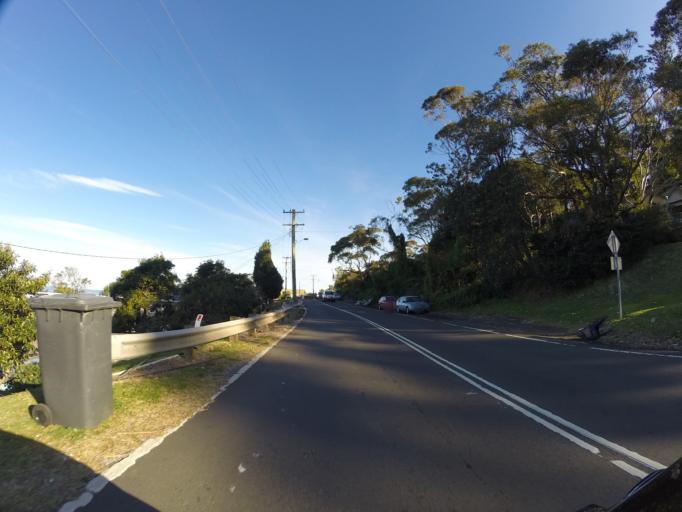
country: AU
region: New South Wales
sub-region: Wollongong
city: Bulli
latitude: -34.2754
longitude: 150.9557
